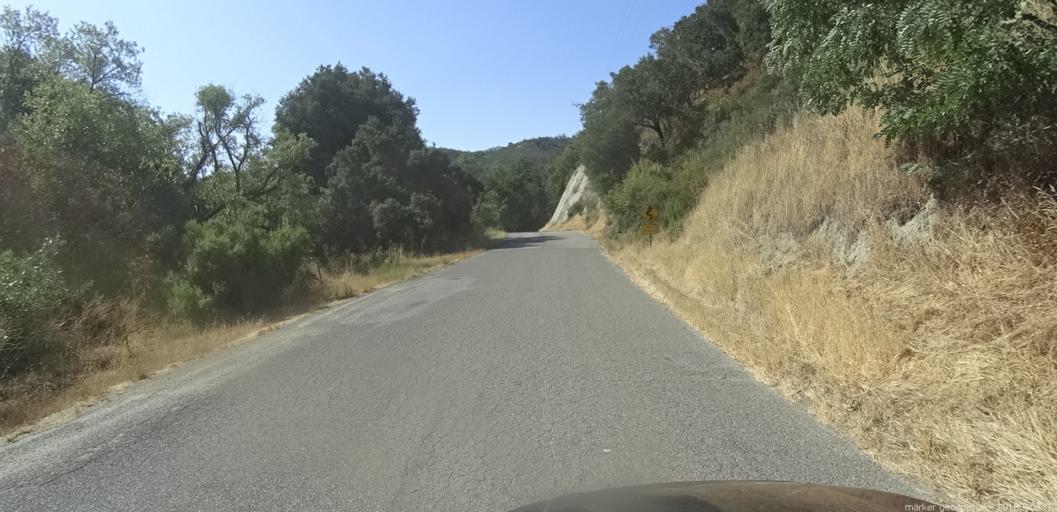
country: US
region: California
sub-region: Monterey County
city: Gonzales
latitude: 36.3974
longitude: -121.5804
